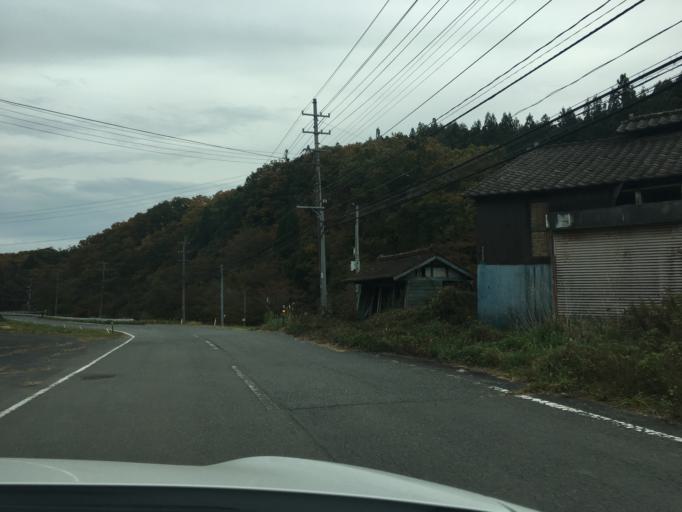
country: JP
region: Fukushima
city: Ishikawa
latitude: 37.2001
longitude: 140.6434
